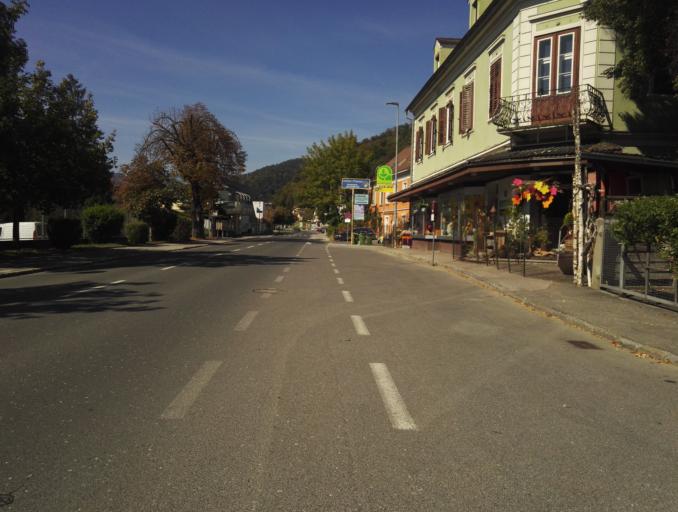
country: AT
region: Styria
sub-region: Politischer Bezirk Graz-Umgebung
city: Gratkorn
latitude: 47.1350
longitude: 15.3360
